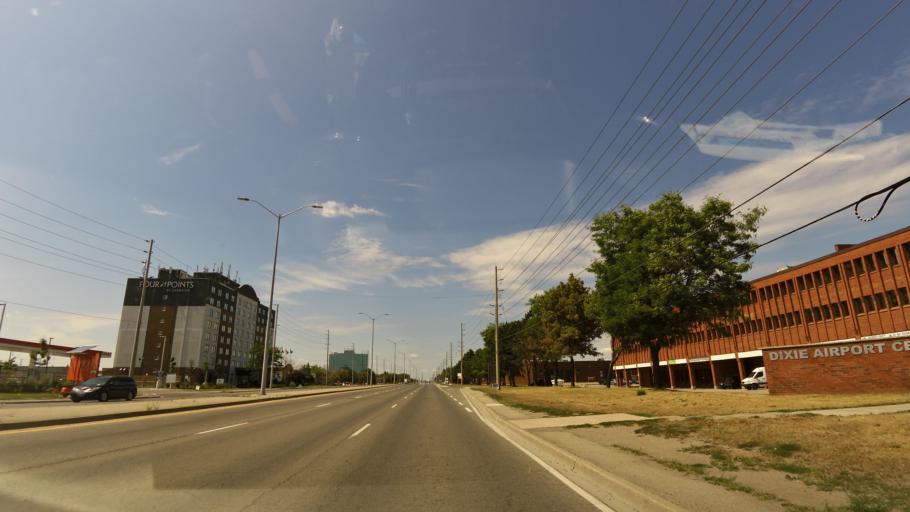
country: CA
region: Ontario
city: Mississauga
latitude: 43.6566
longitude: -79.6492
